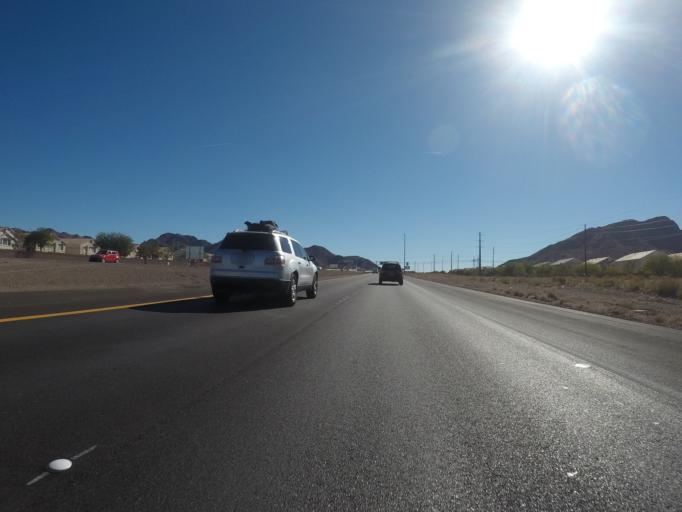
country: US
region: Nevada
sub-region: Clark County
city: Henderson
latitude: 35.9909
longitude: -114.9276
